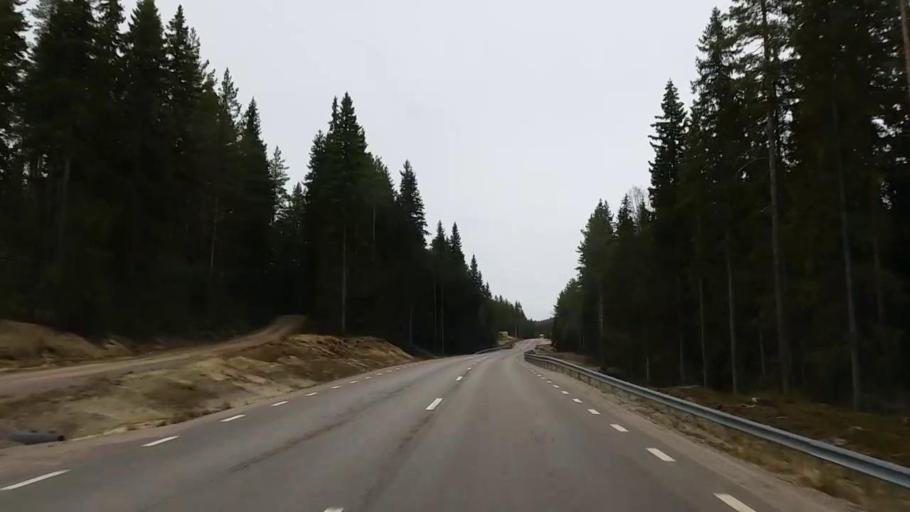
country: SE
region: Gaevleborg
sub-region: Ovanakers Kommun
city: Edsbyn
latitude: 61.1676
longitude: 15.8826
